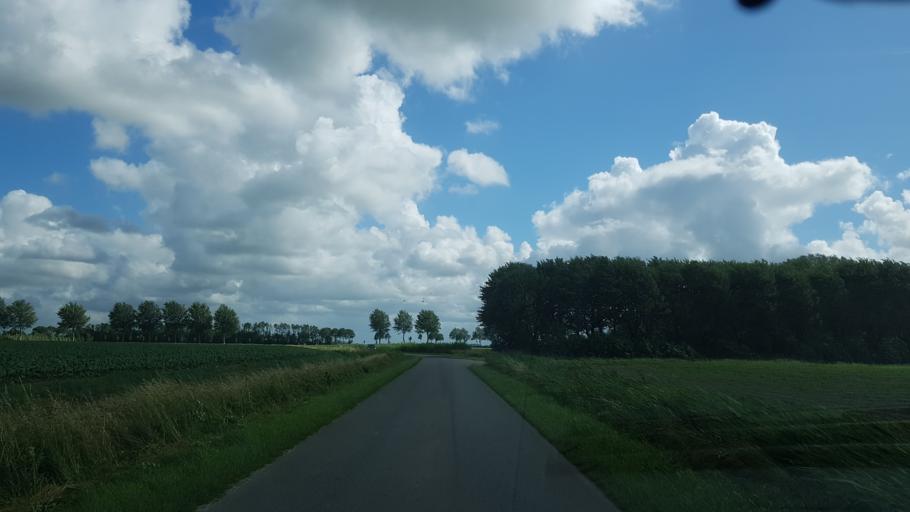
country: NL
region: Groningen
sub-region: Gemeente Bedum
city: Bedum
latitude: 53.4114
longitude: 6.6482
